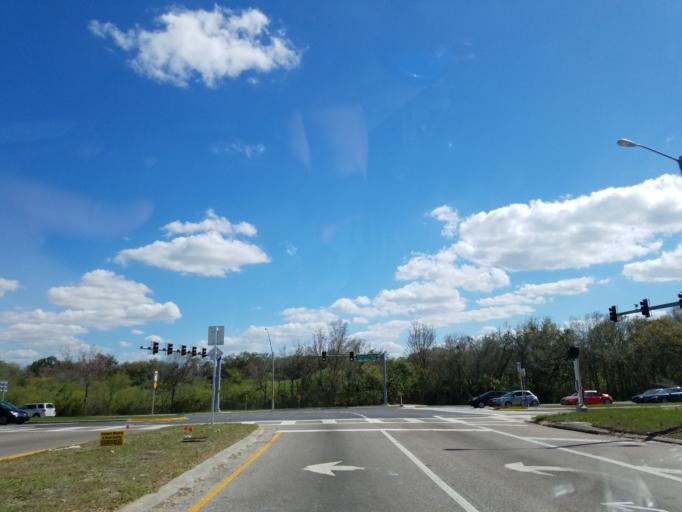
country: US
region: Florida
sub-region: Hillsborough County
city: University
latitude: 28.0800
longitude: -82.4256
